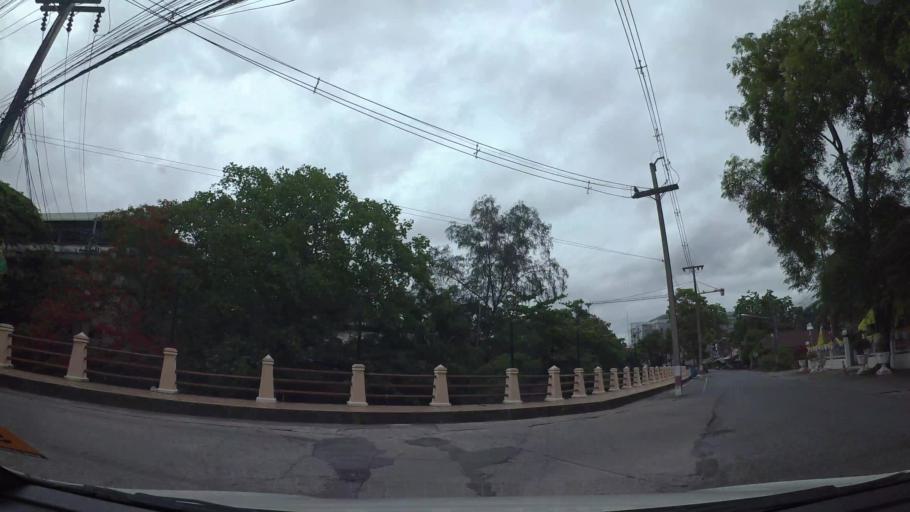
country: TH
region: Rayong
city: Rayong
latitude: 12.6739
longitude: 101.2762
